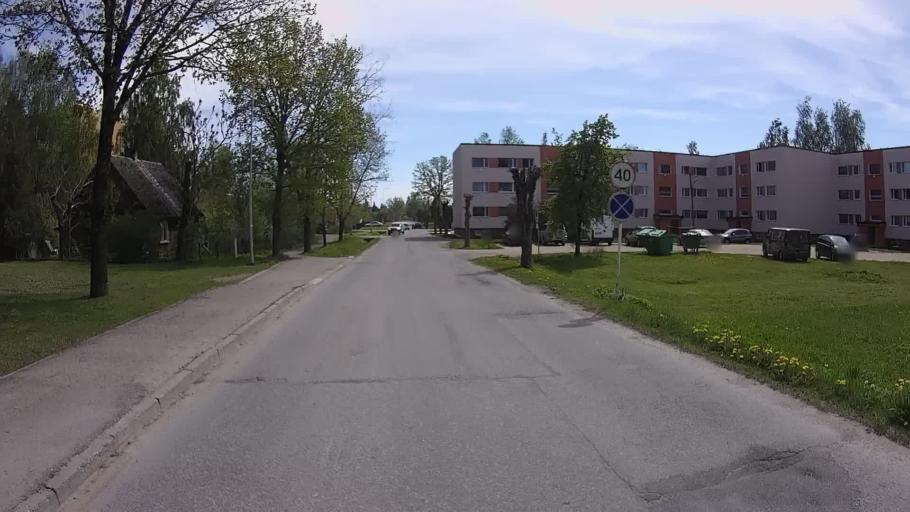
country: EE
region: Valgamaa
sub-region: Valga linn
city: Valga
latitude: 57.7824
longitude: 26.0614
